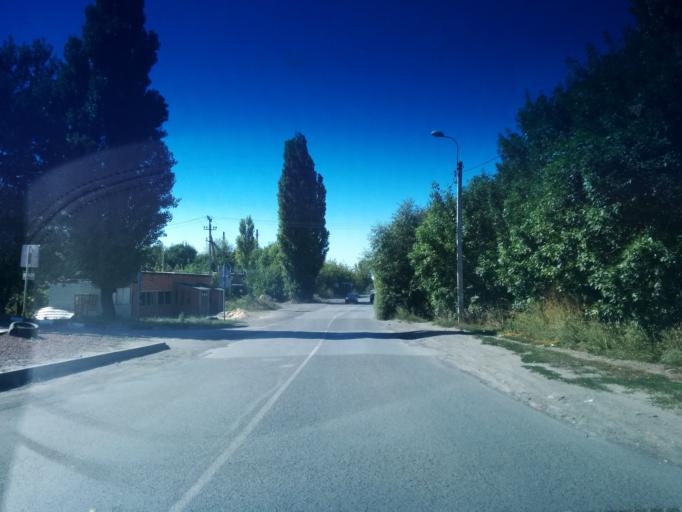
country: RU
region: Rostov
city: Shakhty
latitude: 47.6837
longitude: 40.2744
